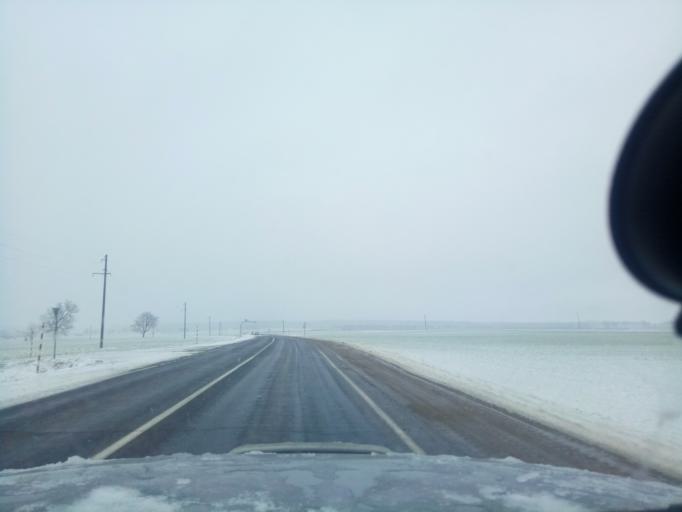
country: BY
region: Minsk
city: Nyasvizh
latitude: 53.2041
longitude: 26.6732
